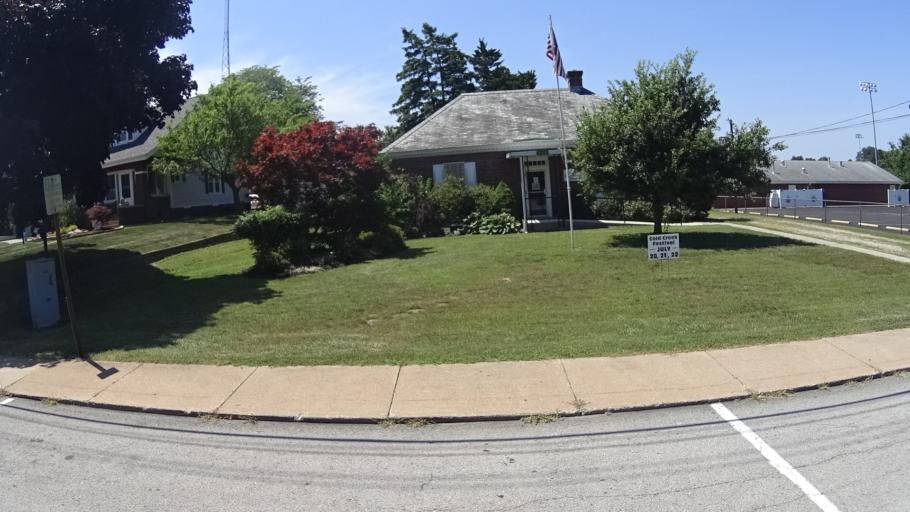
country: US
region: Ohio
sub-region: Erie County
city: Sandusky
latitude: 41.3986
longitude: -82.8020
